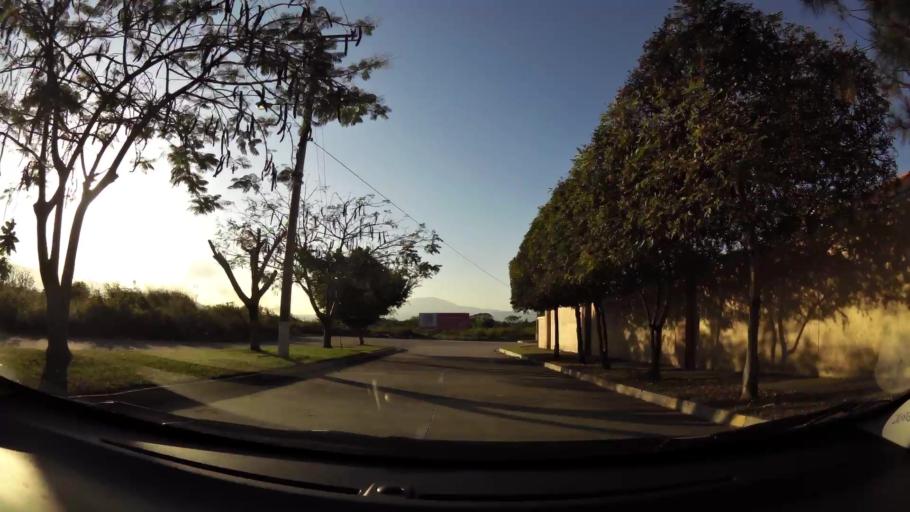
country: SV
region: La Libertad
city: Ciudad Arce
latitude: 13.7564
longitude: -89.3720
